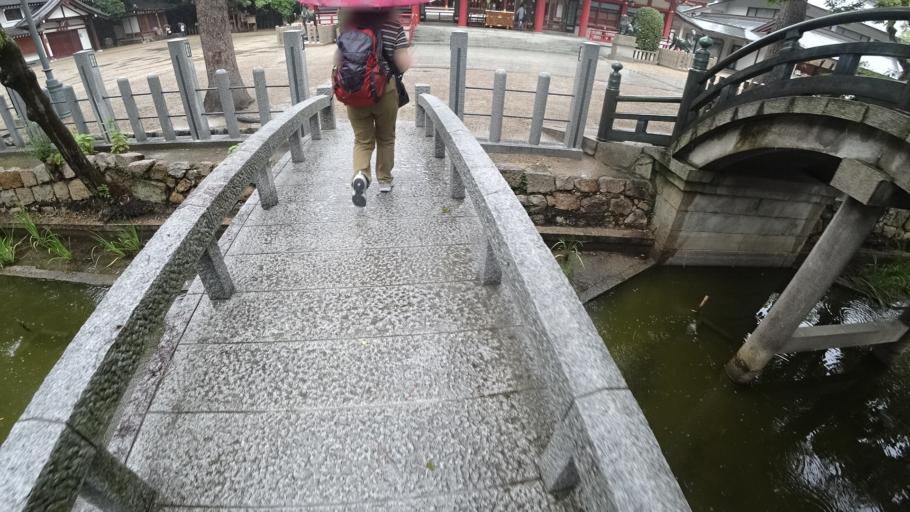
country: JP
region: Hyogo
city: Nishinomiya-hama
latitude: 34.7354
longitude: 135.3345
